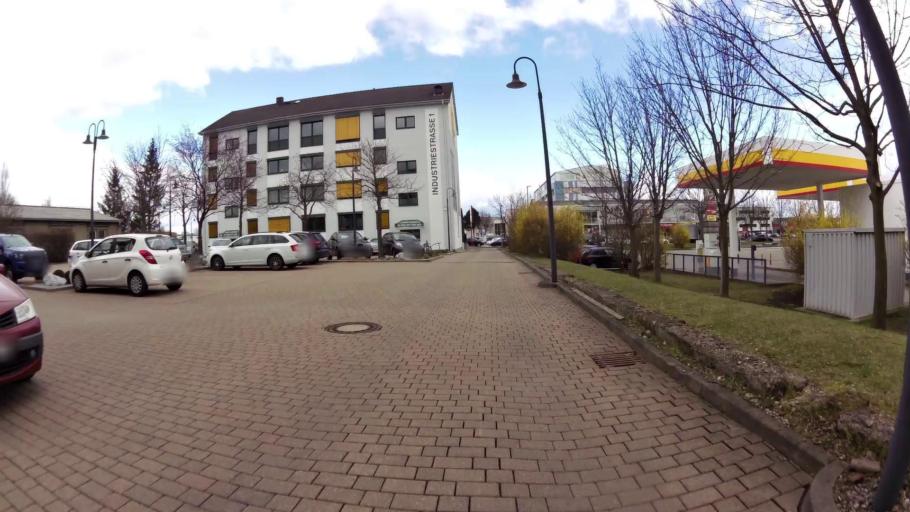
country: DE
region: Thuringia
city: Weimar
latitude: 50.9945
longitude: 11.3259
